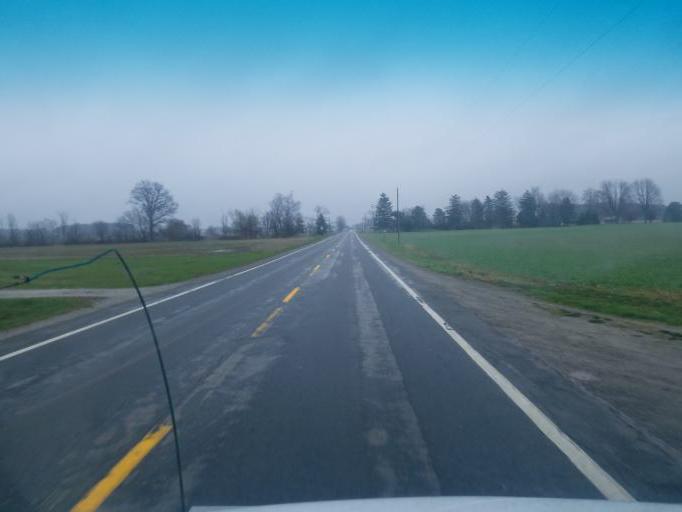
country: US
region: Ohio
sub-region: Wood County
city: Weston
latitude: 41.3722
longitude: -83.7306
